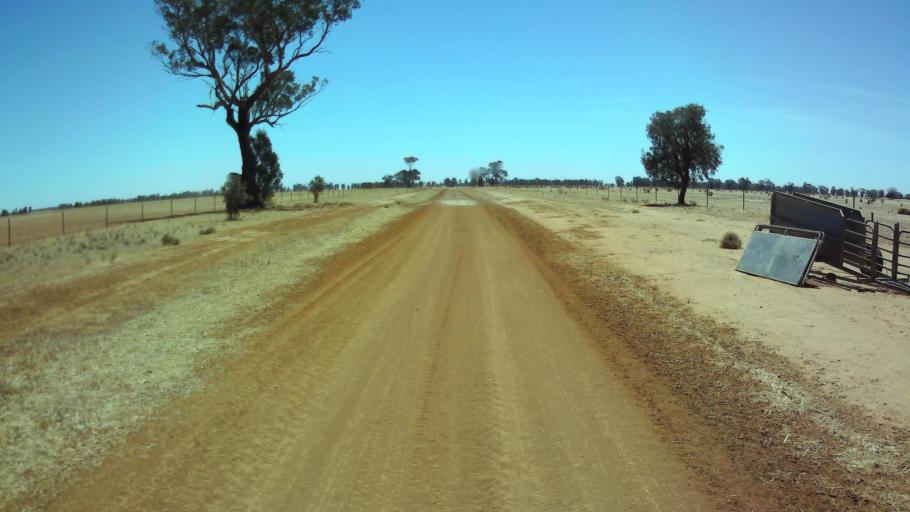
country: AU
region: New South Wales
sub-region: Weddin
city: Grenfell
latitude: -33.9906
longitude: 147.7342
